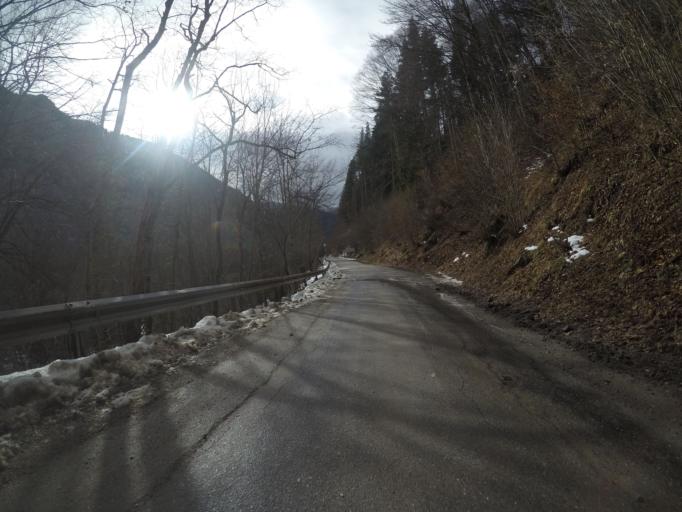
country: BG
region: Kyustendil
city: Sapareva Banya
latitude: 42.1369
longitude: 23.3439
